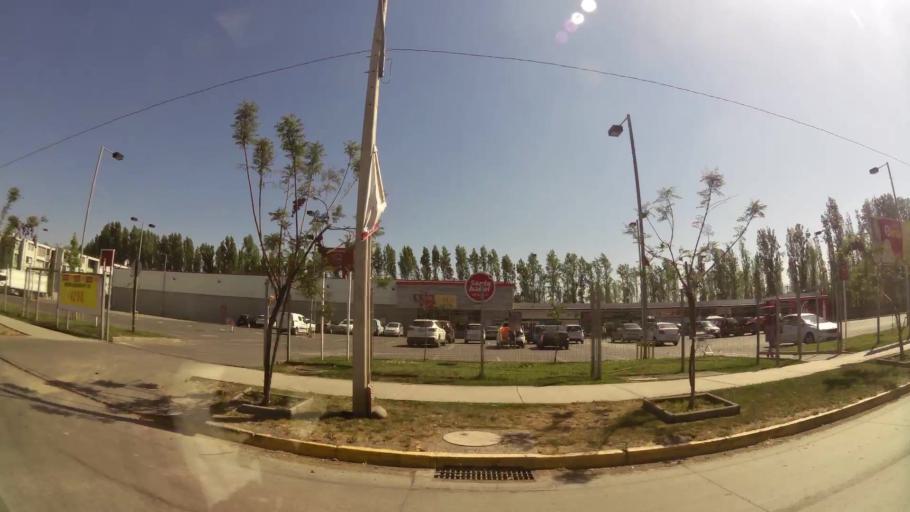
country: CL
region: Santiago Metropolitan
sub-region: Provincia de Maipo
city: San Bernardo
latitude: -33.6160
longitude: -70.6838
